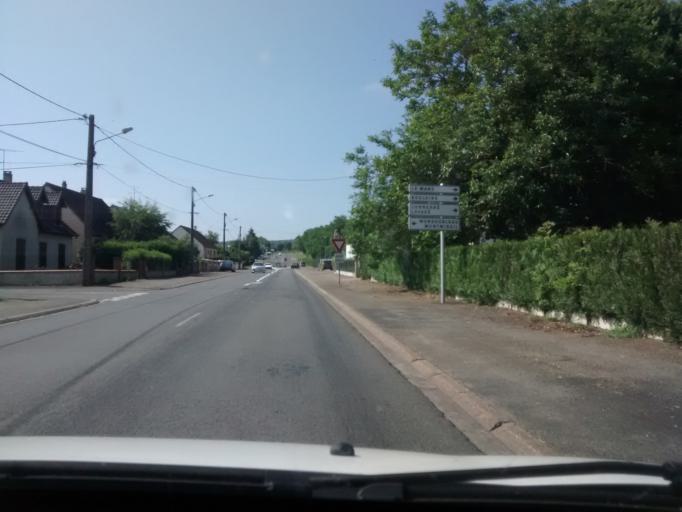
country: FR
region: Pays de la Loire
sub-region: Departement de la Sarthe
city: Vibraye
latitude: 48.0615
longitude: 0.7284
